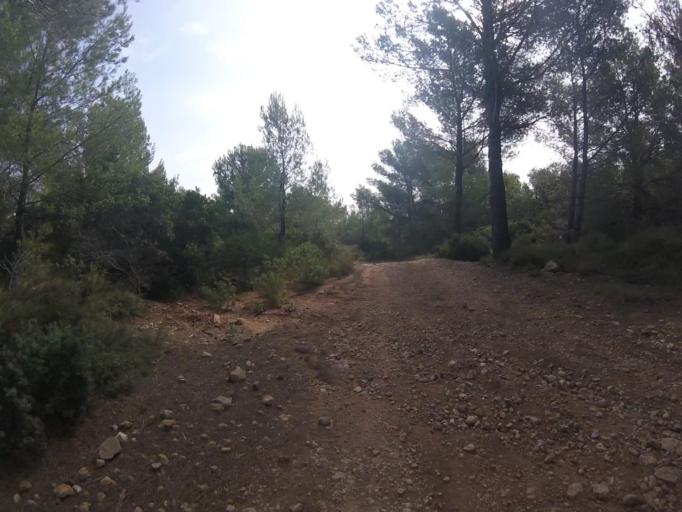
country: ES
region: Valencia
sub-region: Provincia de Castello
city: Benicassim
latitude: 40.0866
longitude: 0.0436
